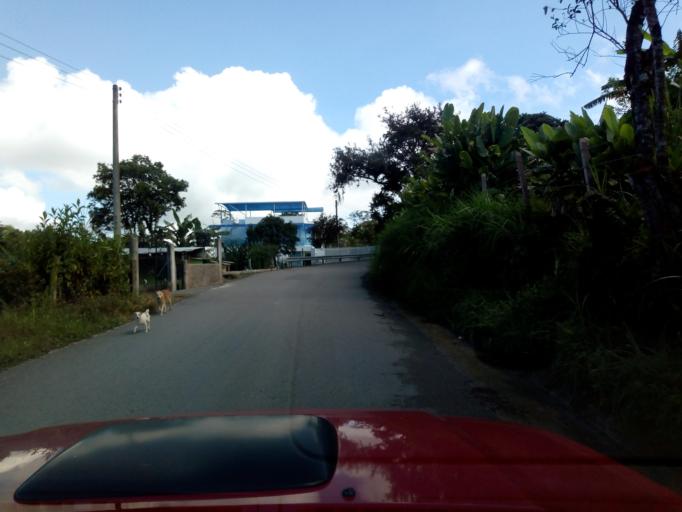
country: CO
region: Boyaca
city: Moniquira
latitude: 5.8819
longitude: -73.5450
